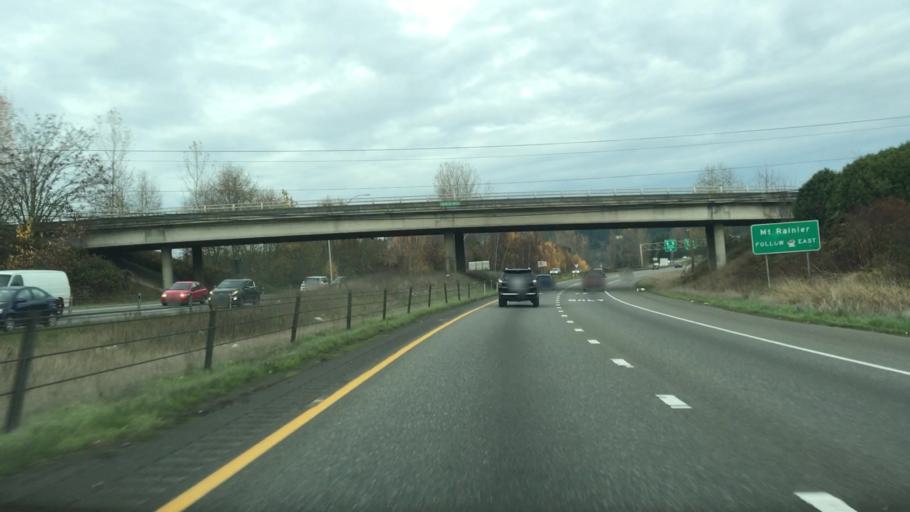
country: US
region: Washington
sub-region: Pierce County
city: North Puyallup
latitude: 47.1960
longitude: -122.2822
